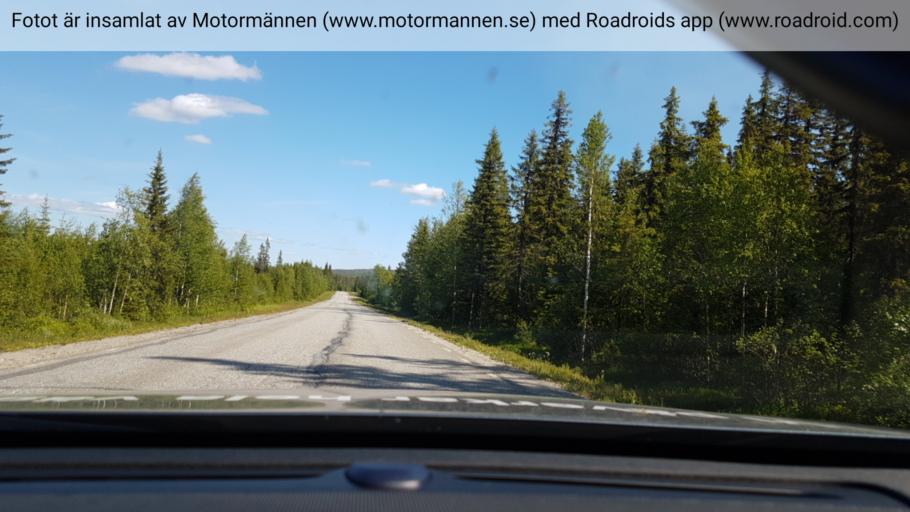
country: SE
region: Vaesterbotten
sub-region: Lycksele Kommun
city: Soderfors
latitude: 64.6355
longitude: 17.9041
